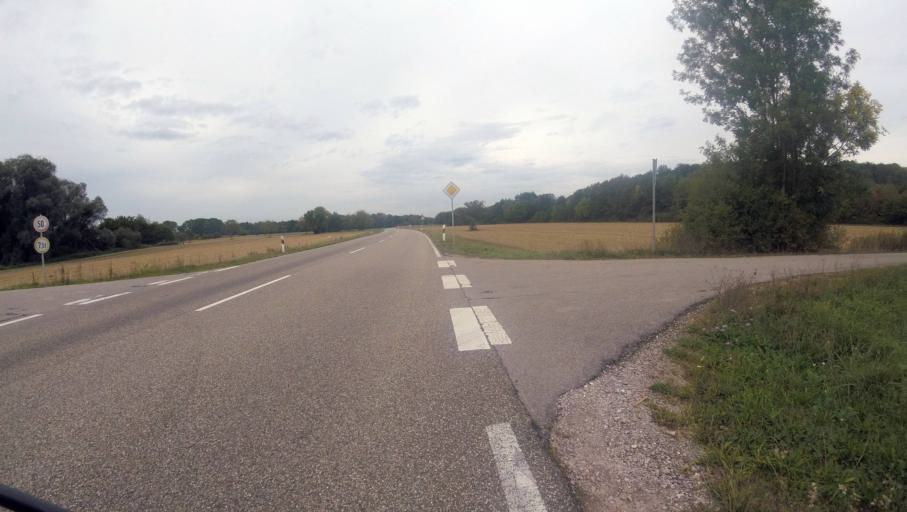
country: DE
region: Baden-Wuerttemberg
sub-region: Karlsruhe Region
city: Iffezheim
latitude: 48.8373
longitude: 8.1585
